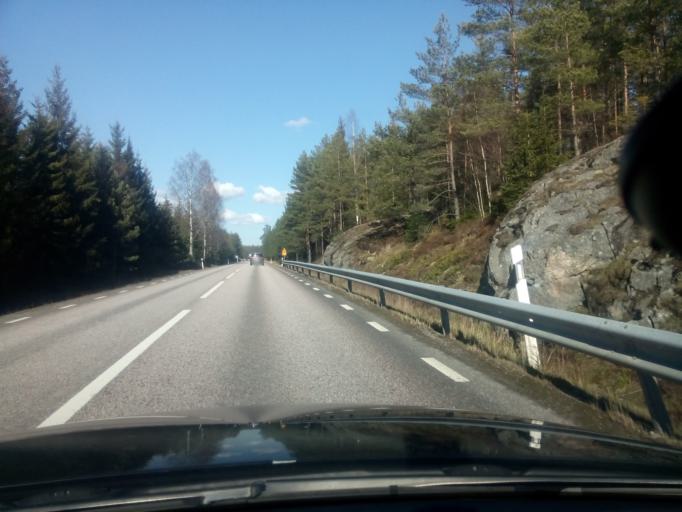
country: SE
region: Soedermanland
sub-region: Strangnas Kommun
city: Akers Styckebruk
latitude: 59.2207
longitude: 16.9093
